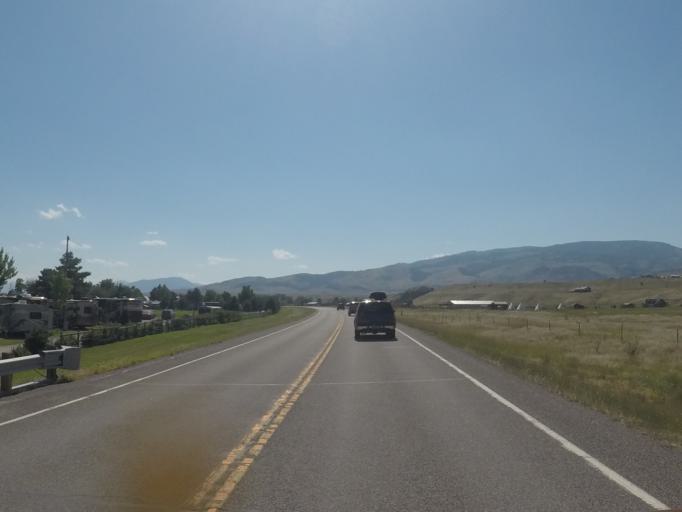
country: US
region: Montana
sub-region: Park County
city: Livingston
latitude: 45.4184
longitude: -110.6806
